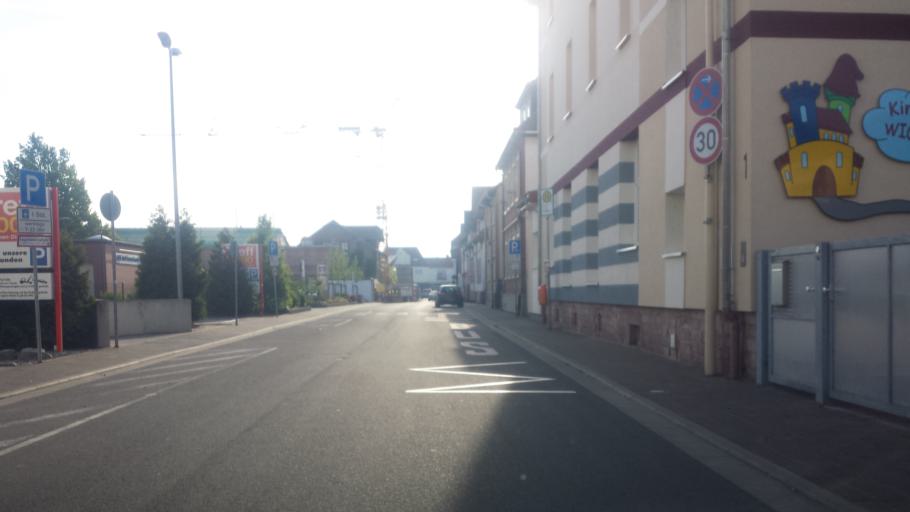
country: DE
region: Hesse
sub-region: Regierungsbezirk Darmstadt
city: Burstadt
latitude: 49.6407
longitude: 8.4550
